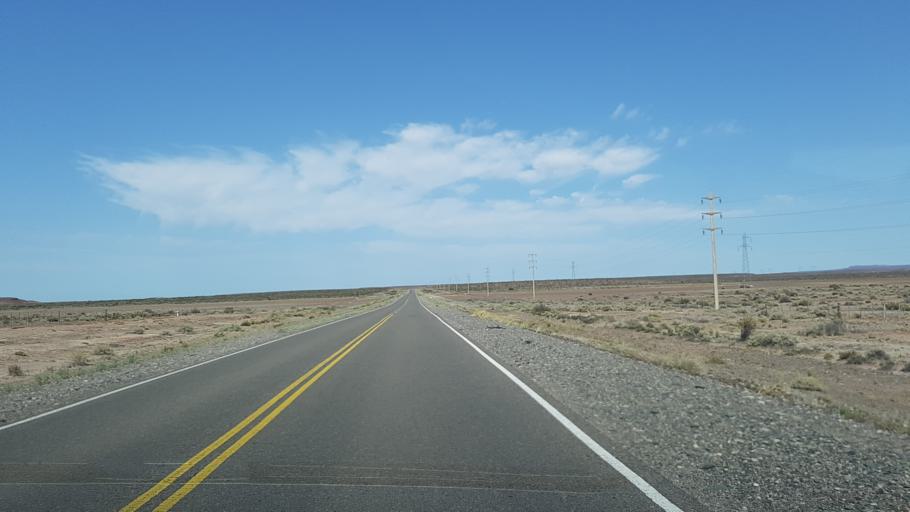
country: AR
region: Neuquen
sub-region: Departamento de Picun Leufu
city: Picun Leufu
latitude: -39.4097
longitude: -69.1439
